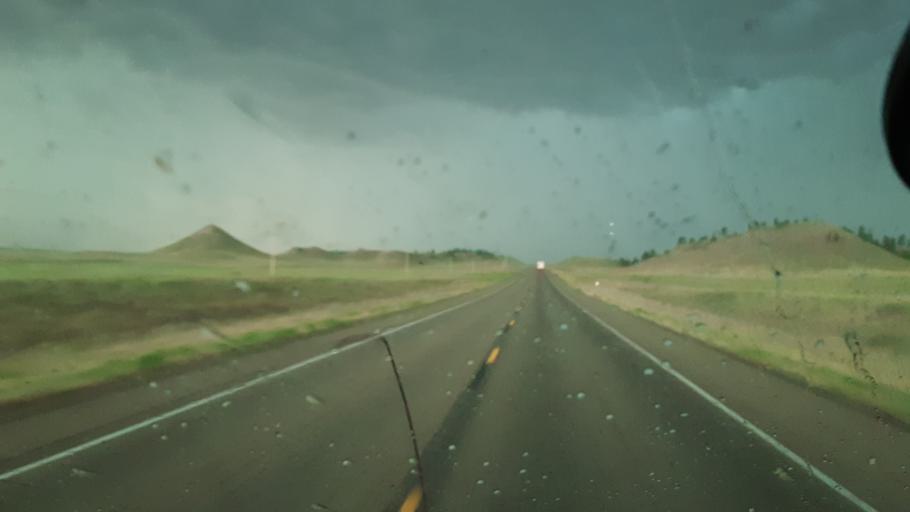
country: US
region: Montana
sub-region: Powder River County
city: Broadus
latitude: 45.4710
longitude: -105.4853
